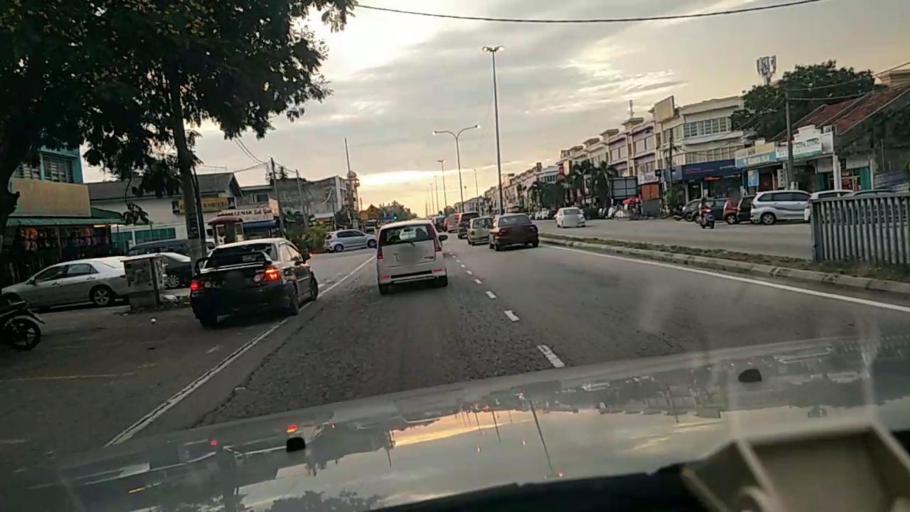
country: MY
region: Perak
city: Kampong Dungun
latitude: 3.1378
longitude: 101.3725
